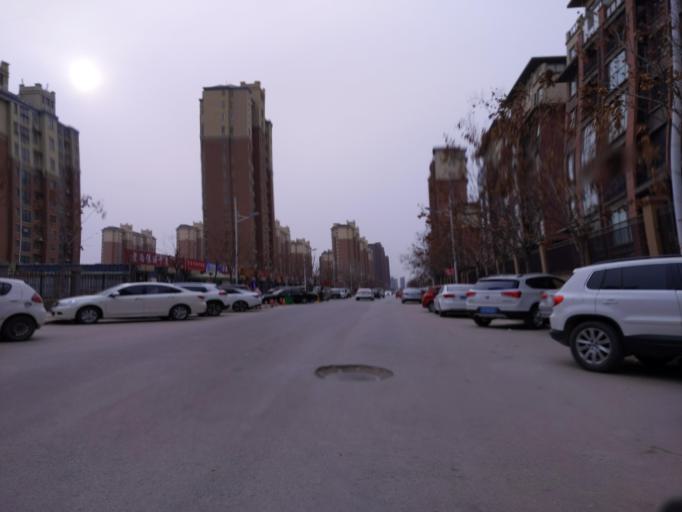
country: CN
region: Henan Sheng
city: Zhongyuanlu
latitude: 35.7420
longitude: 115.0773
